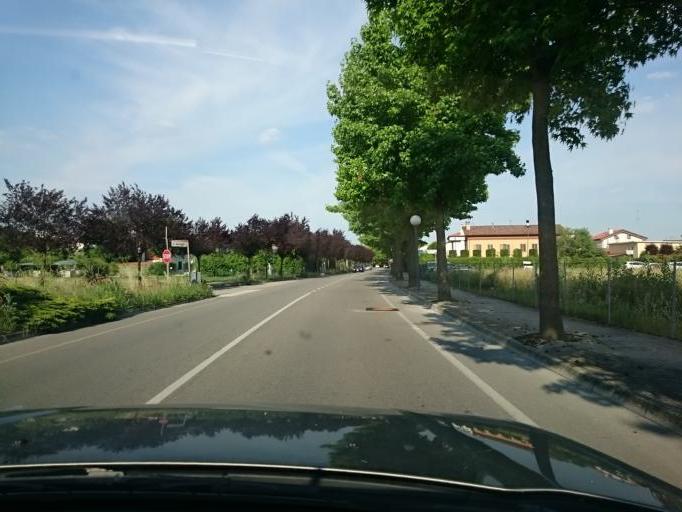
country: IT
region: Veneto
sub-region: Provincia di Padova
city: Montegrotto Terme
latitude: 45.3330
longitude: 11.7765
